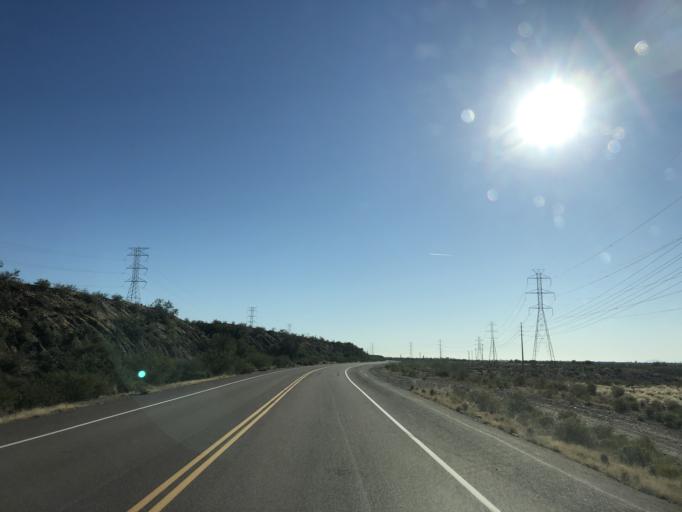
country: US
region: Arizona
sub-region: Maricopa County
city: Sun City West
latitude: 33.6930
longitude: -112.2942
